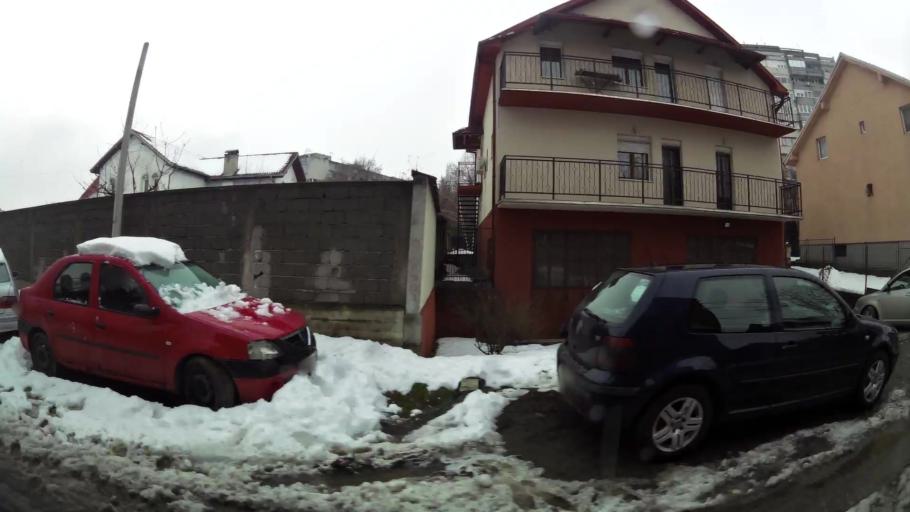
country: RS
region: Central Serbia
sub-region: Belgrade
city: Zemun
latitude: 44.8452
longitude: 20.3896
